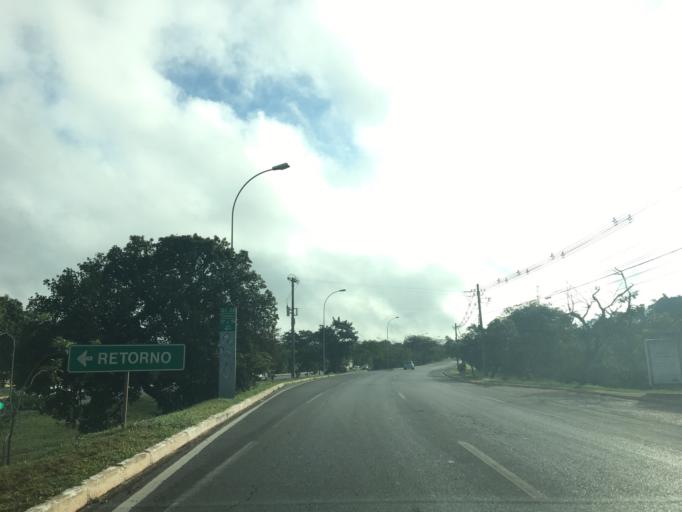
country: BR
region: Federal District
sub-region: Brasilia
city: Brasilia
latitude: -15.8129
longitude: -47.8051
